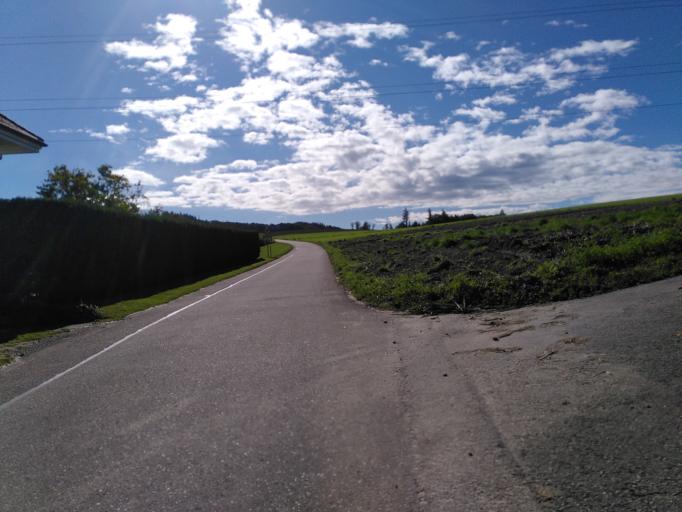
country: CH
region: Bern
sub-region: Oberaargau
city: Seeberg
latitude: 47.1386
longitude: 7.7142
